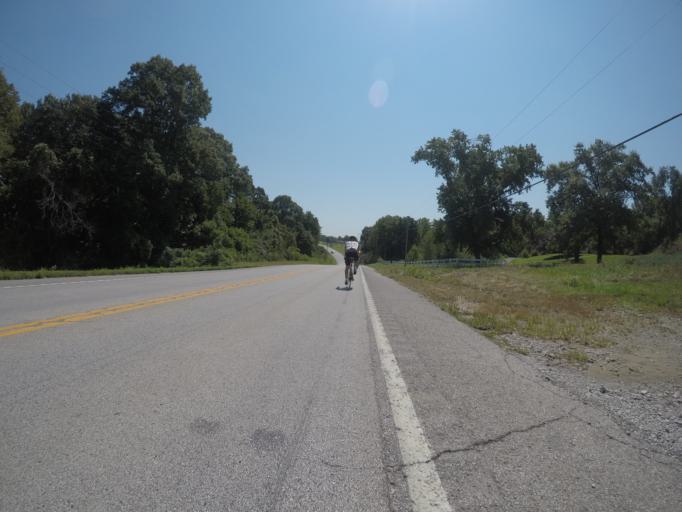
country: US
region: Missouri
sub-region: Platte County
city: Weston
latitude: 39.4261
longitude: -94.9063
